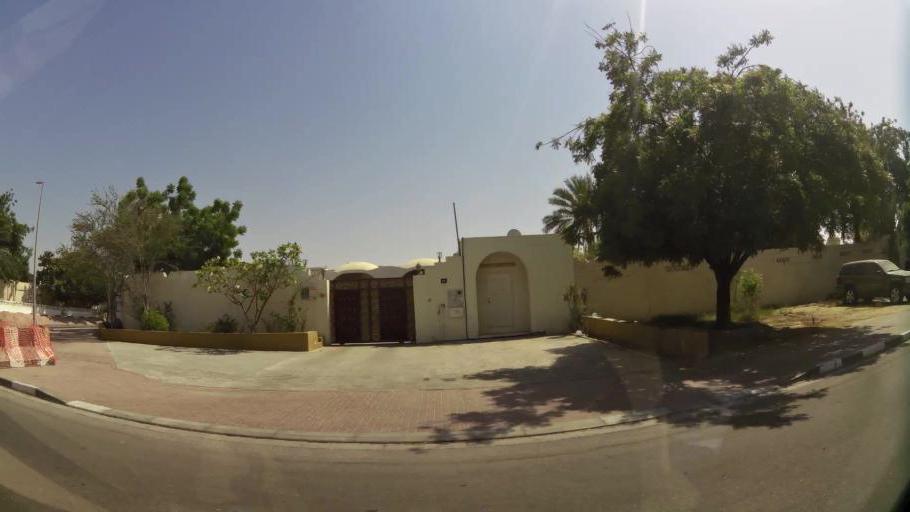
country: AE
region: Ash Shariqah
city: Sharjah
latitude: 25.2701
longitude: 55.3647
